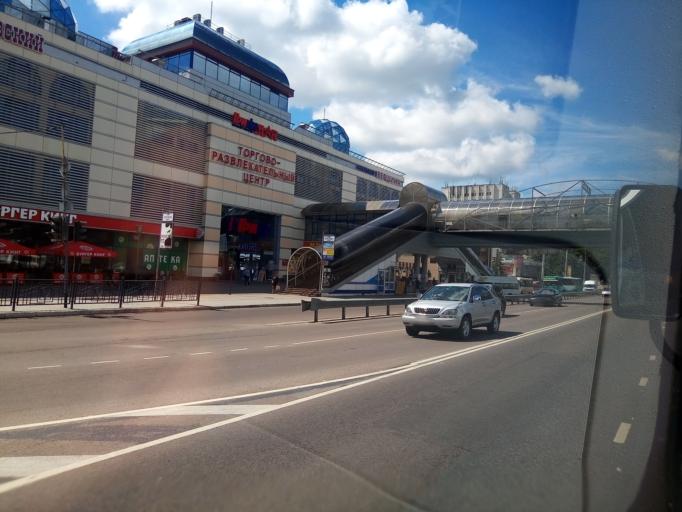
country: RU
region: Kursk
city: Kursk
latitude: 51.7276
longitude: 36.1862
